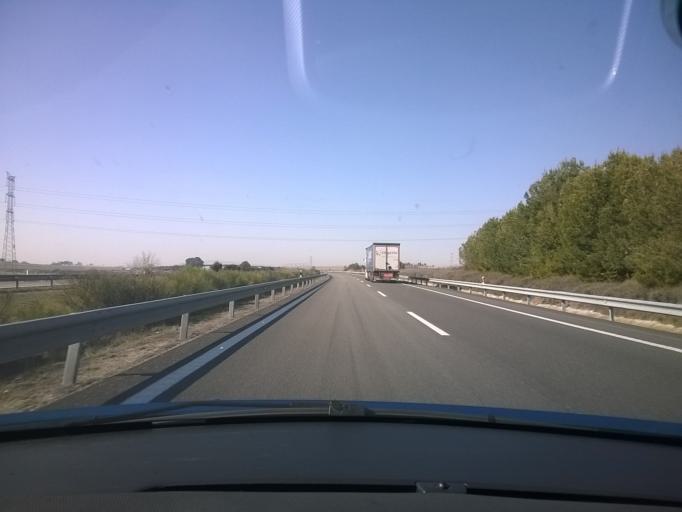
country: ES
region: Aragon
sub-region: Provincia de Huesca
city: Penalba
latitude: 41.5159
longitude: -0.0795
